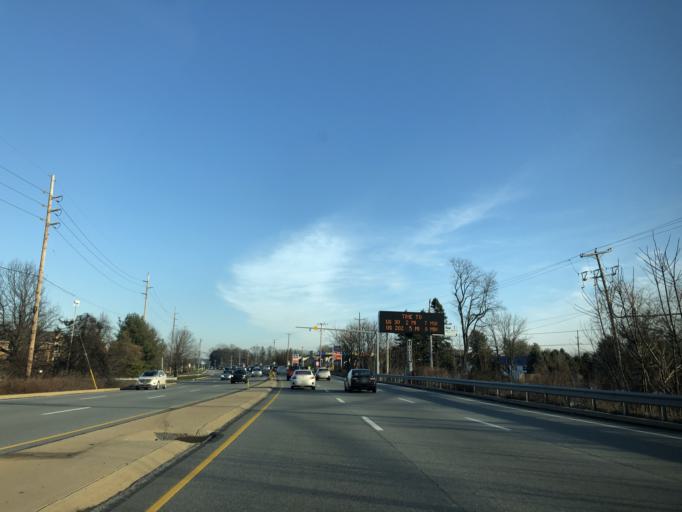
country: US
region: Pennsylvania
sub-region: Chester County
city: Exton
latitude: 40.0562
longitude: -75.6542
